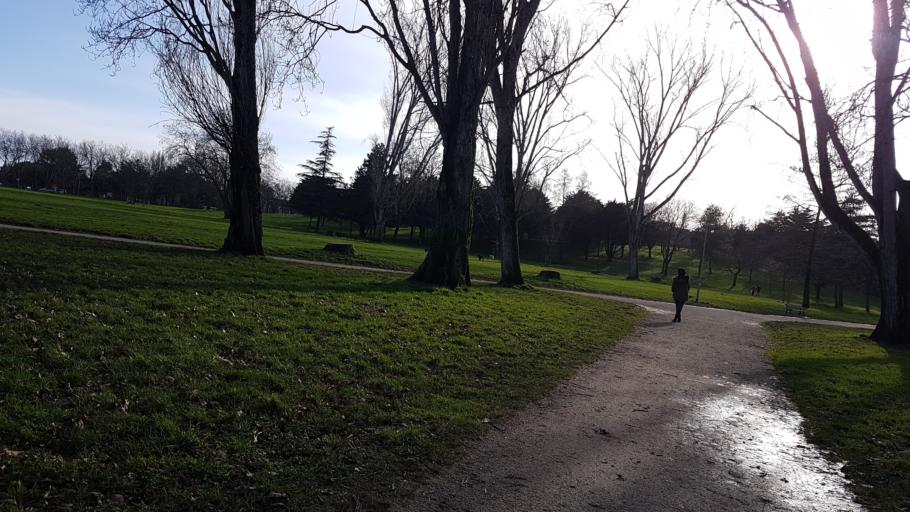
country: FR
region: Pays de la Loire
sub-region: Departement de la Loire-Atlantique
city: Saint-Nazaire
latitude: 47.2729
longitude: -2.2245
